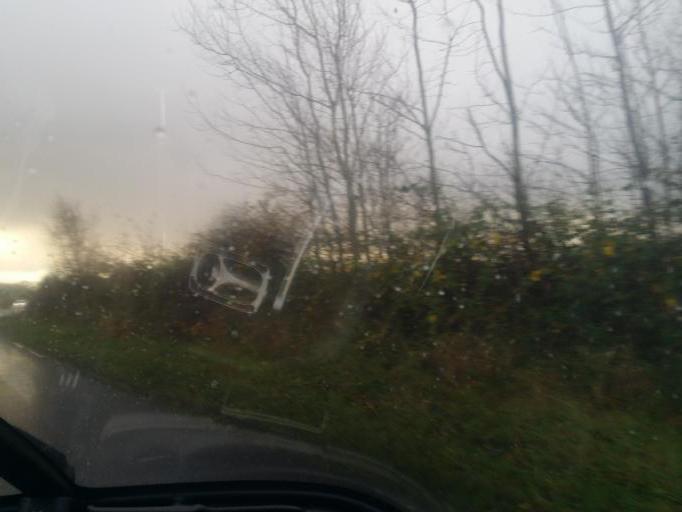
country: DE
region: Schleswig-Holstein
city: Immenstedt
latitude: 54.1622
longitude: 9.3033
